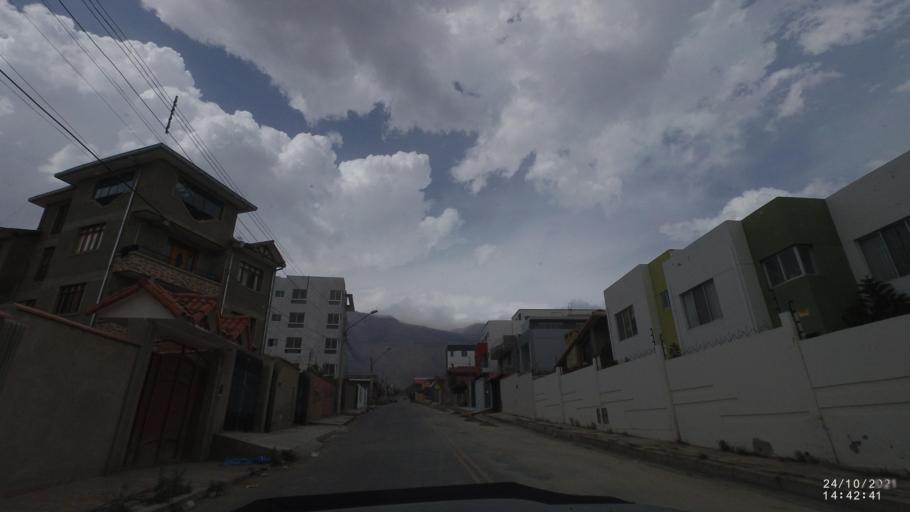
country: BO
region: Cochabamba
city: Cochabamba
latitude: -17.3511
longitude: -66.1777
